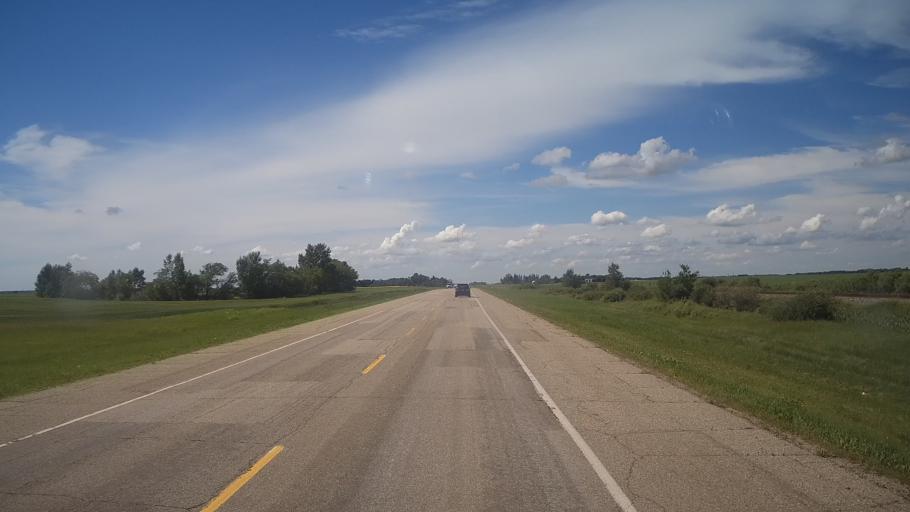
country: CA
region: Saskatchewan
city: Yorkton
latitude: 51.0847
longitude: -102.2519
